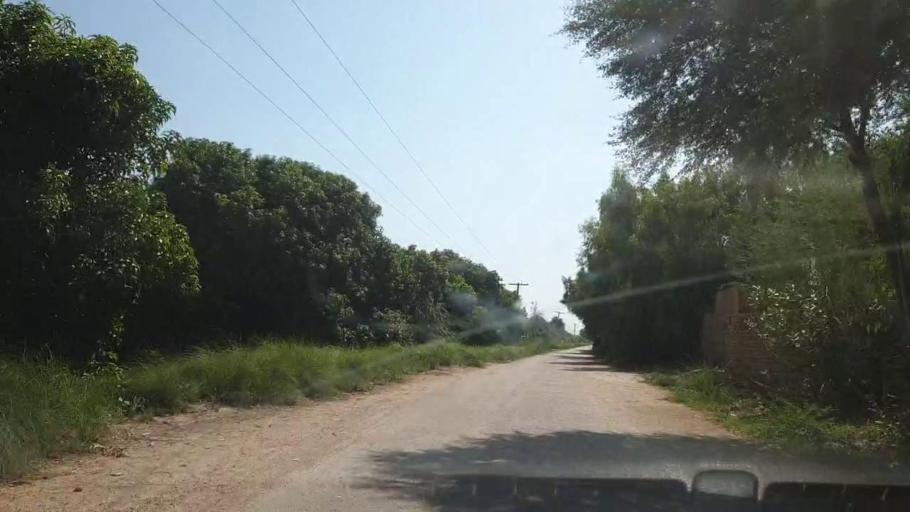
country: PK
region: Sindh
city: Tando Jam
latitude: 25.4385
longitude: 68.5848
